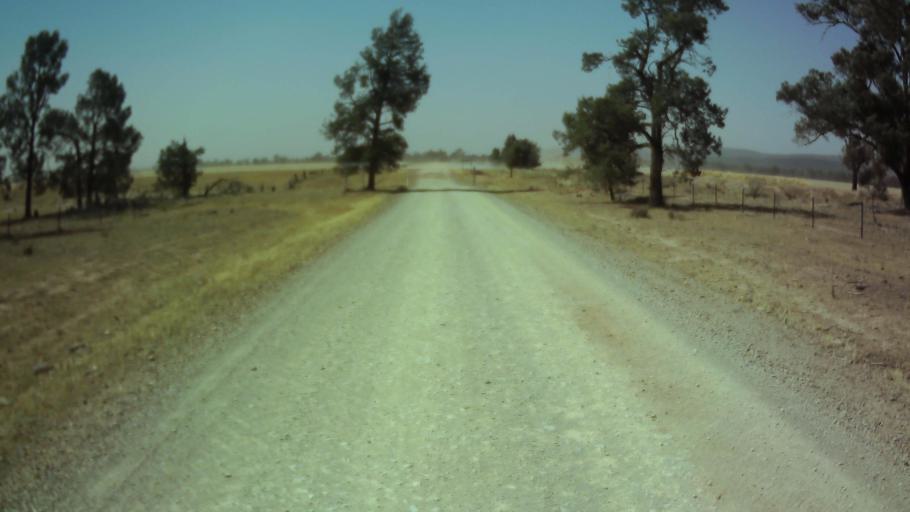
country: AU
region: New South Wales
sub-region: Weddin
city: Grenfell
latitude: -34.0168
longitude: 147.9152
